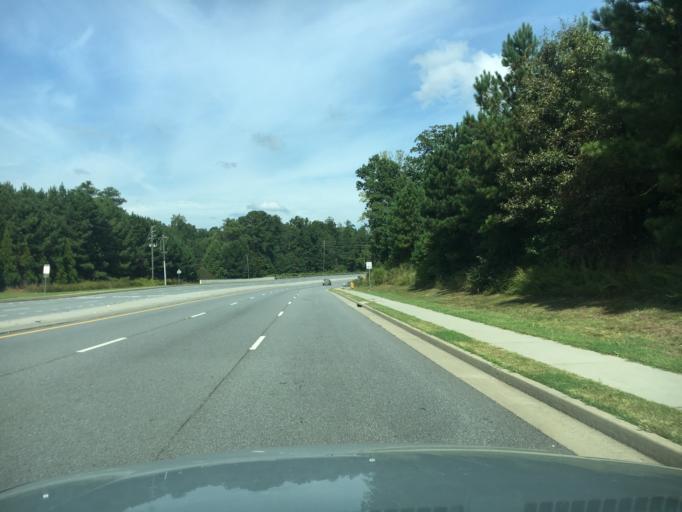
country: US
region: Georgia
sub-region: Gwinnett County
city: Duluth
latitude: 33.9866
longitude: -84.1600
